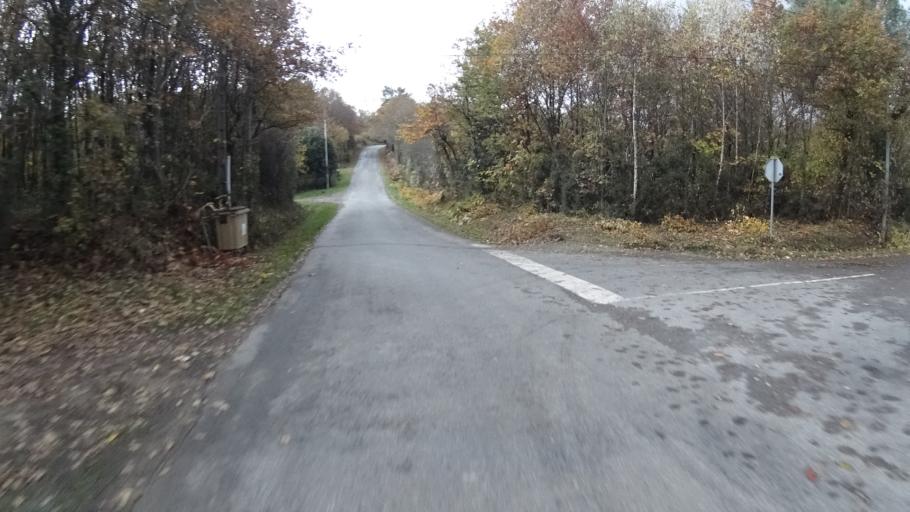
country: FR
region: Pays de la Loire
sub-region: Departement de la Loire-Atlantique
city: Avessac
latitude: 47.6600
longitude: -2.0217
